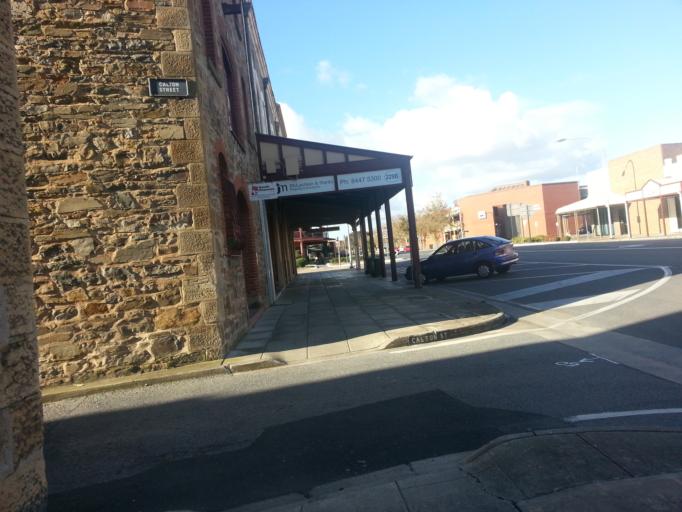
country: AU
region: South Australia
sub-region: Port Adelaide Enfield
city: Birkenhead
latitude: -34.8441
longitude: 138.5059
